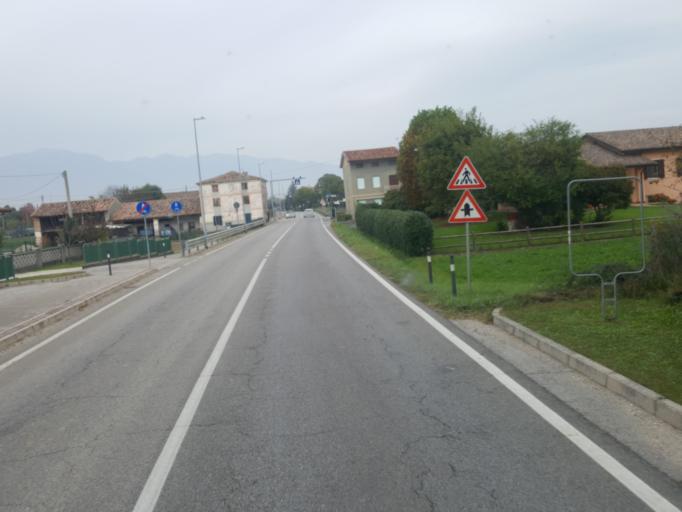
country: IT
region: Veneto
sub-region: Provincia di Treviso
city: Loria Bessica
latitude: 45.7414
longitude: 11.8664
